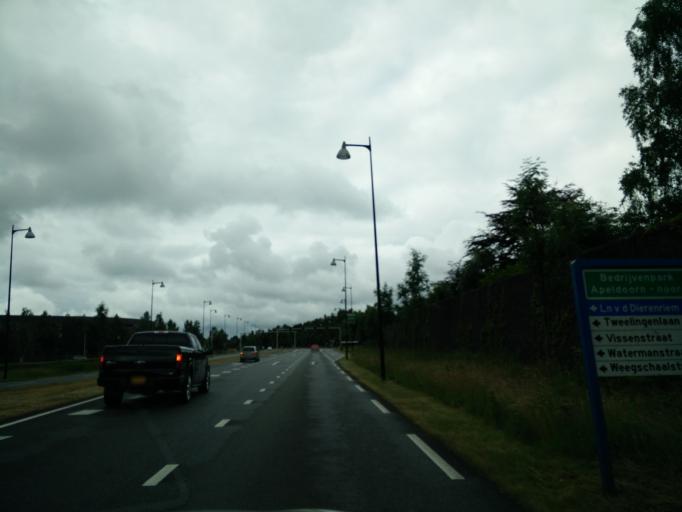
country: NL
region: Gelderland
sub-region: Gemeente Apeldoorn
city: Apeldoorn
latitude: 52.2404
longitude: 5.9799
